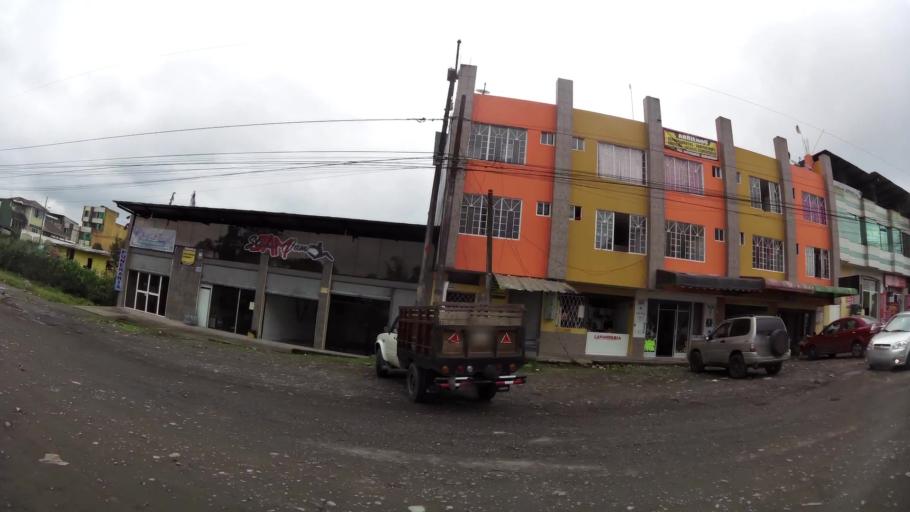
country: EC
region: Santo Domingo de los Tsachilas
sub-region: Canton Santo Domingo de los Colorados
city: Santo Domingo de los Colorados
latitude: -0.2464
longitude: -79.1607
